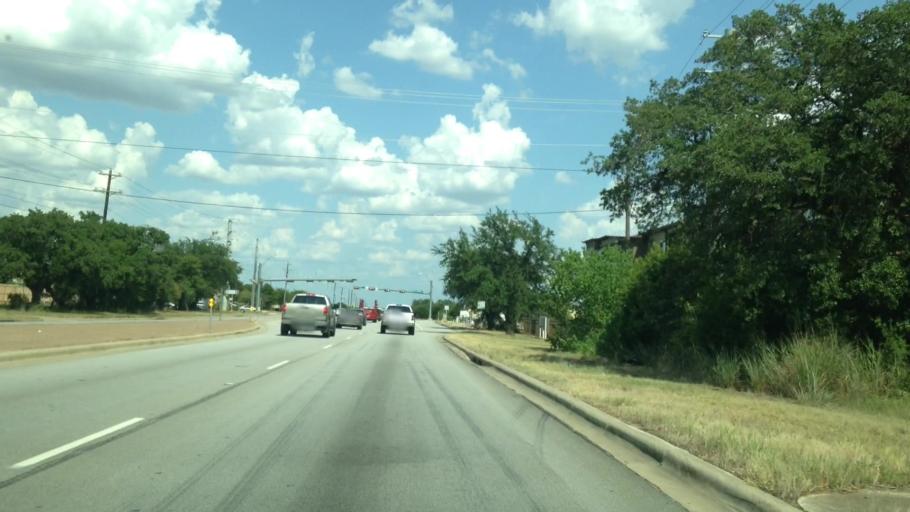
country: US
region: Texas
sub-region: Williamson County
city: Georgetown
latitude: 30.6328
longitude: -97.7025
